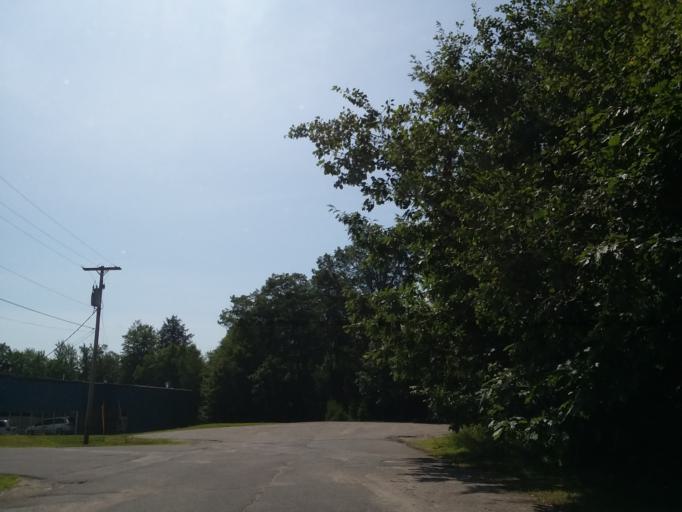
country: US
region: Maine
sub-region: Kennebec County
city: Winthrop
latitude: 44.2821
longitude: -69.9979
